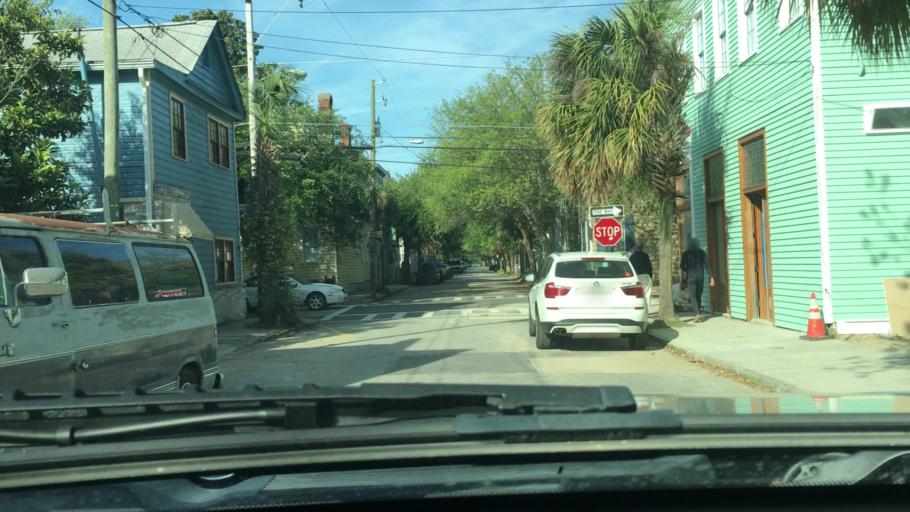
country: US
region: South Carolina
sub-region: Charleston County
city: Charleston
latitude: 32.7932
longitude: -79.9440
